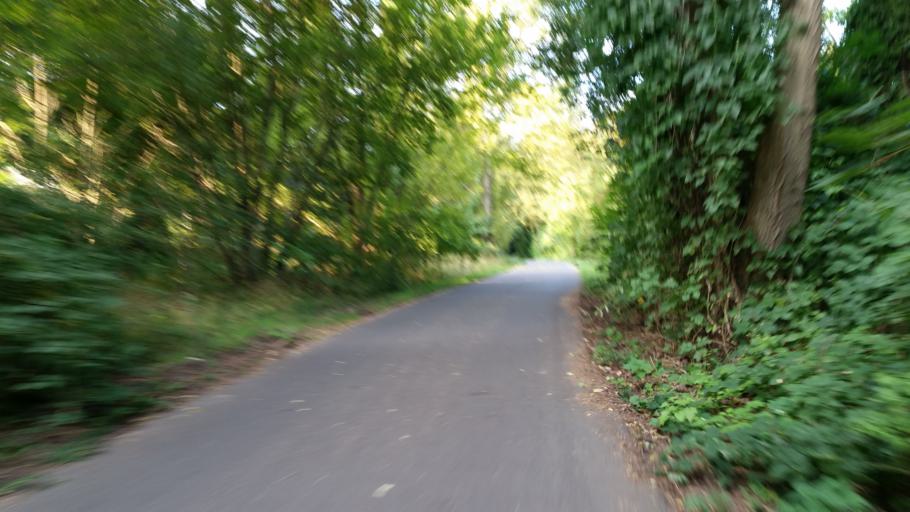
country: DE
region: Brandenburg
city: Teltow
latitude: 52.4083
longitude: 13.2833
